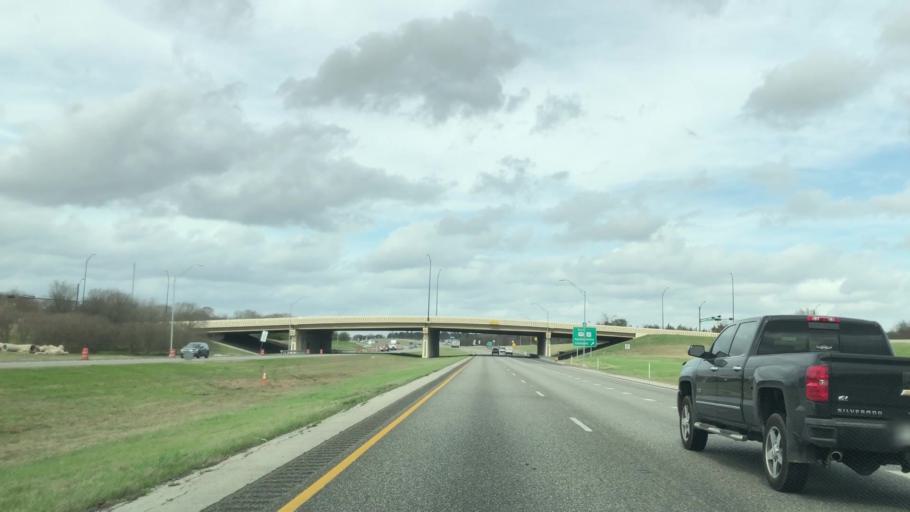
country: US
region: Texas
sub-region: Brazos County
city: Bryan
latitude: 30.6865
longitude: -96.3485
